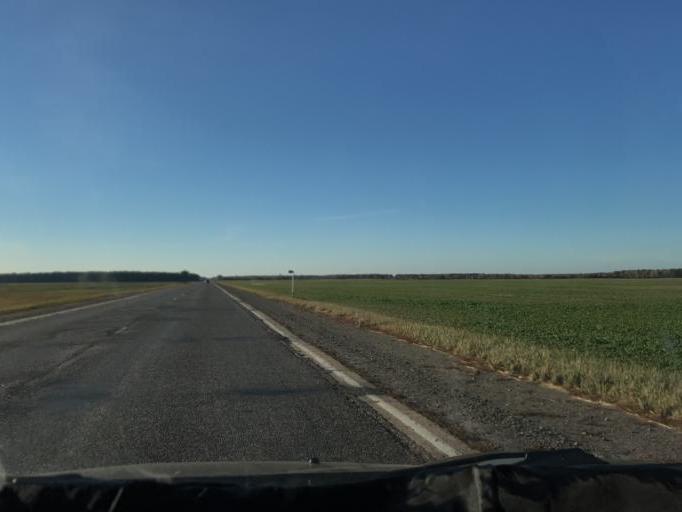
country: BY
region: Gomel
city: Mazyr
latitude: 52.2209
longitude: 29.0063
